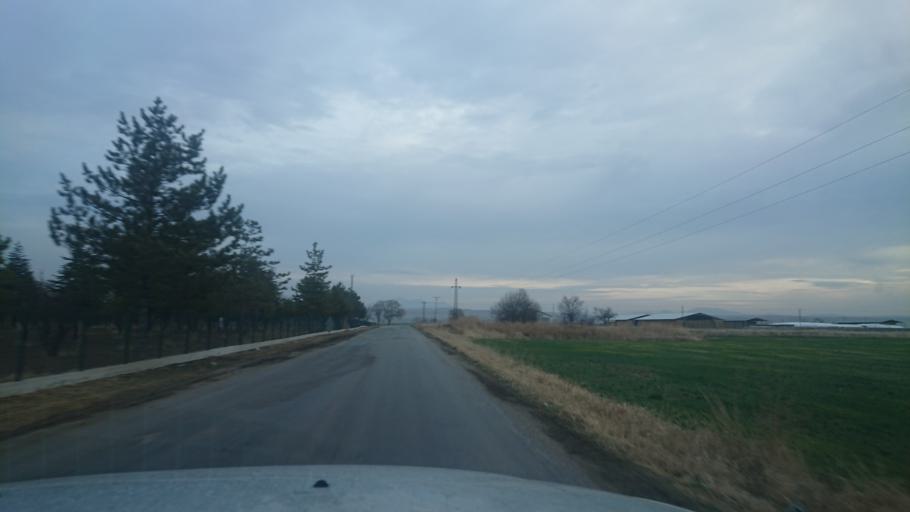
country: TR
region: Aksaray
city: Yesilova
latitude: 38.4579
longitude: 33.8417
